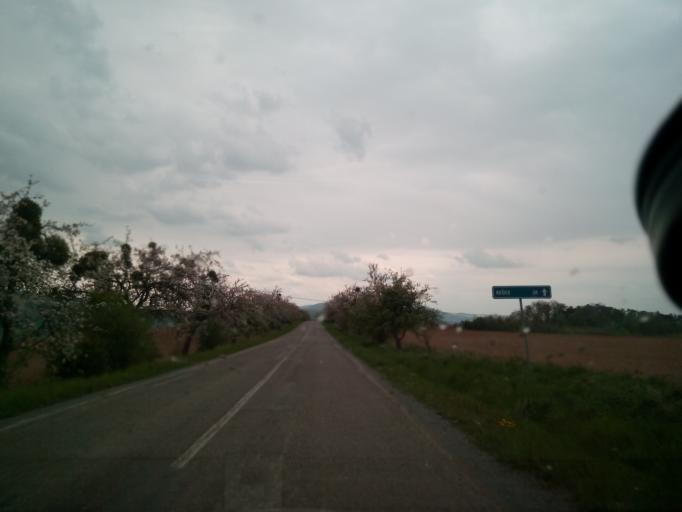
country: SK
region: Kosicky
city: Secovce
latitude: 48.7607
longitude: 21.4653
